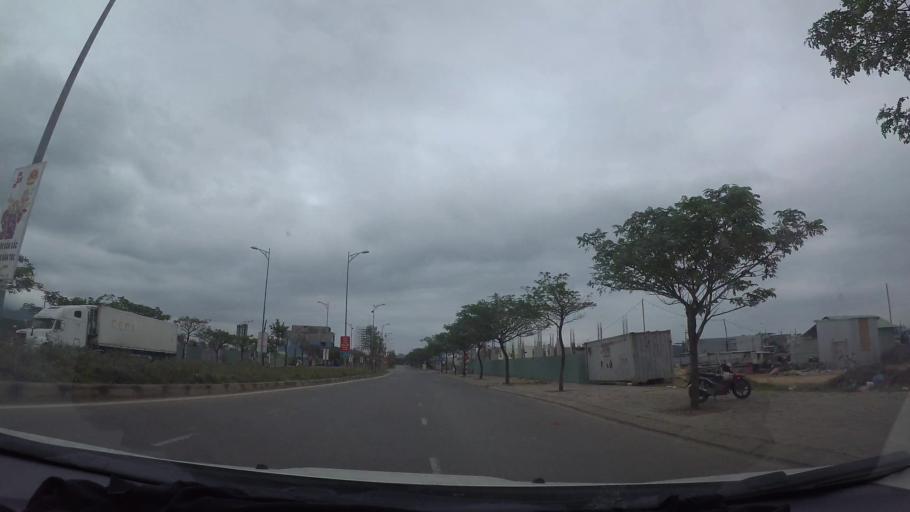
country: VN
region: Da Nang
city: Lien Chieu
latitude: 16.1050
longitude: 108.1238
